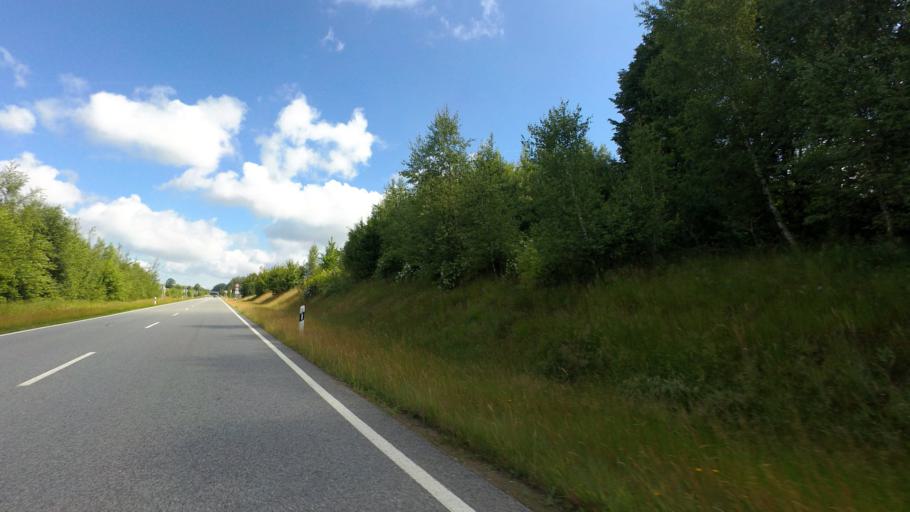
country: DE
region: Saxony
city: Berthelsdorf
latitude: 51.0446
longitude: 14.2130
